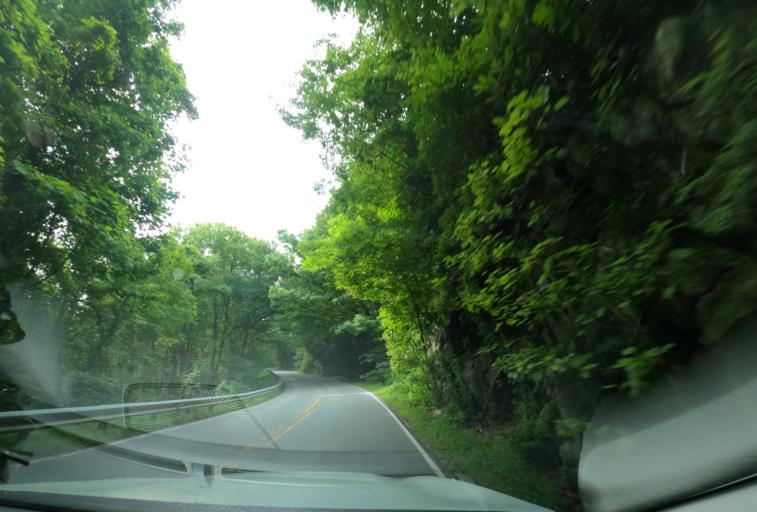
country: US
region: North Carolina
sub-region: Jackson County
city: Cullowhee
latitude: 35.1015
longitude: -83.1509
